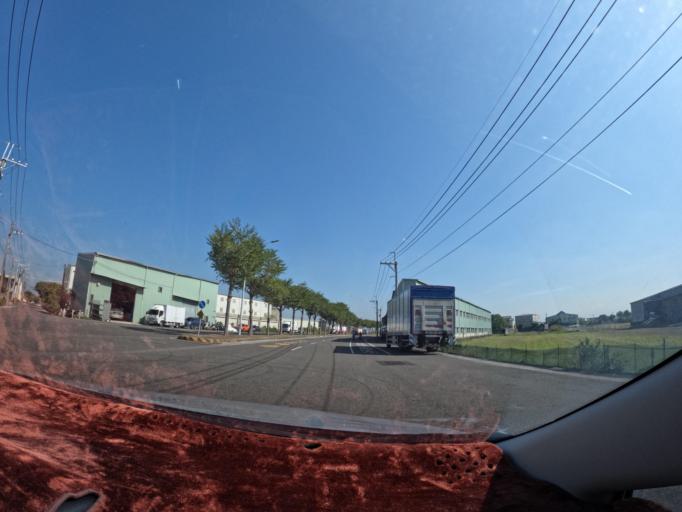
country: TW
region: Taiwan
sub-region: Tainan
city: Tainan
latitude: 23.0062
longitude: 120.2772
